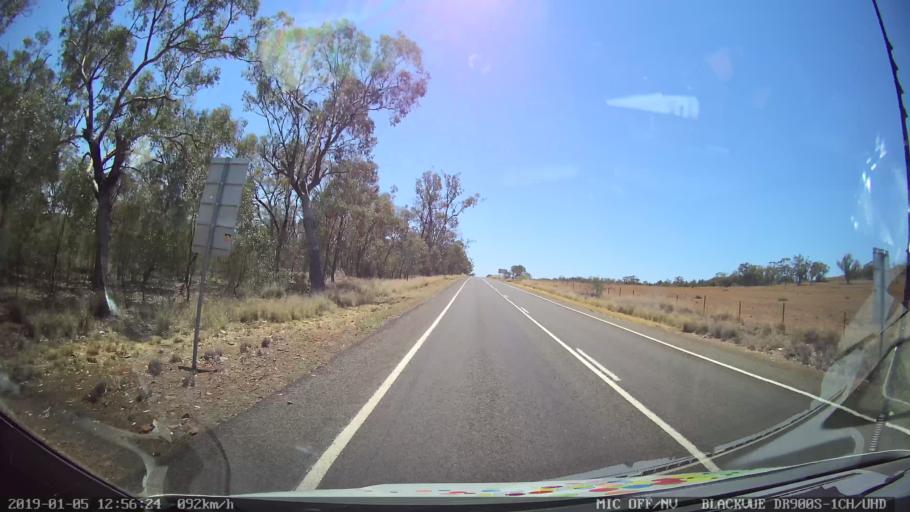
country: AU
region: New South Wales
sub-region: Warrumbungle Shire
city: Coonabarabran
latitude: -31.1144
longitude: 149.7195
